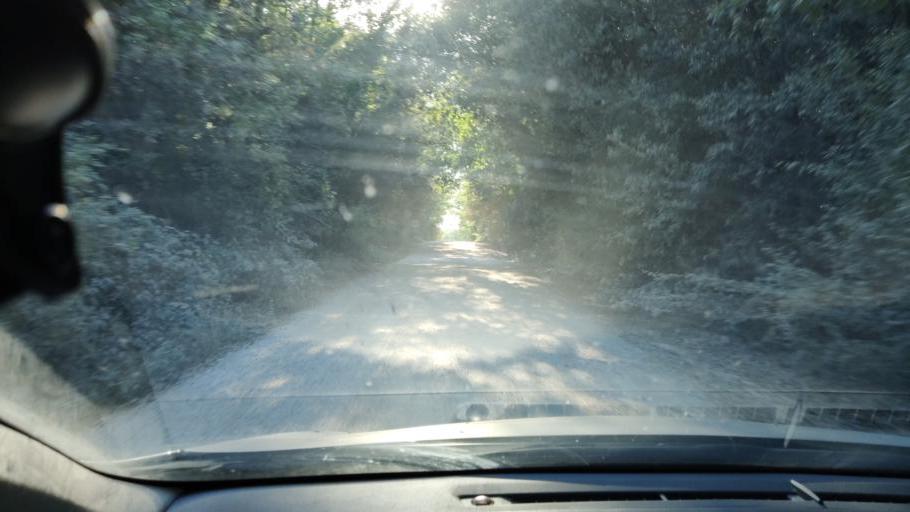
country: IT
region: Umbria
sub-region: Provincia di Terni
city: Penna in Teverina
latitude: 42.5395
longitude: 12.3710
